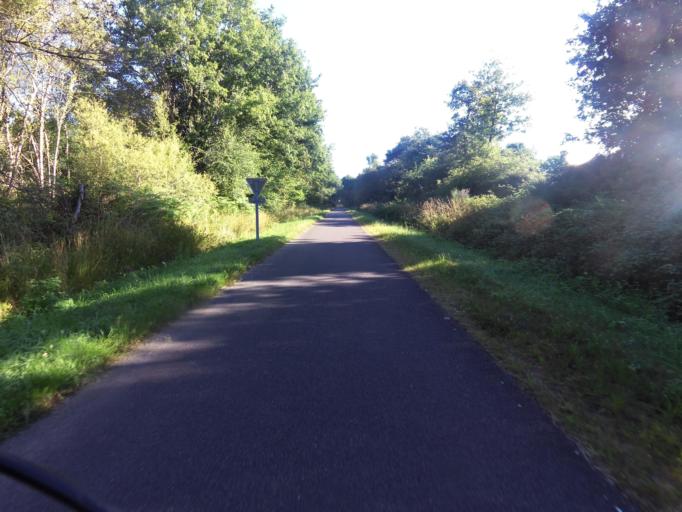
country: FR
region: Brittany
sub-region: Departement du Morbihan
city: Guillac
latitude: 47.8826
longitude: -2.4367
